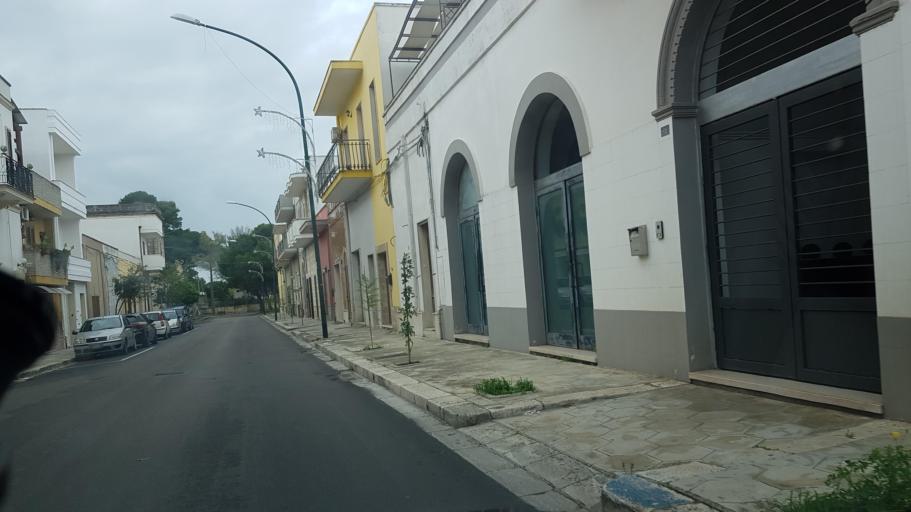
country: IT
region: Apulia
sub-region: Provincia di Lecce
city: Campi Salentina
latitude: 40.3948
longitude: 18.0198
